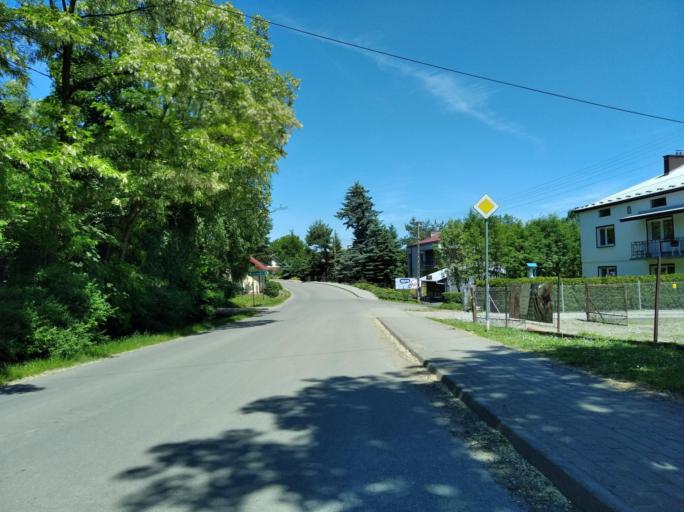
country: PL
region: Subcarpathian Voivodeship
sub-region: Powiat jasielski
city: Tarnowiec
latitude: 49.7127
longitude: 21.5543
